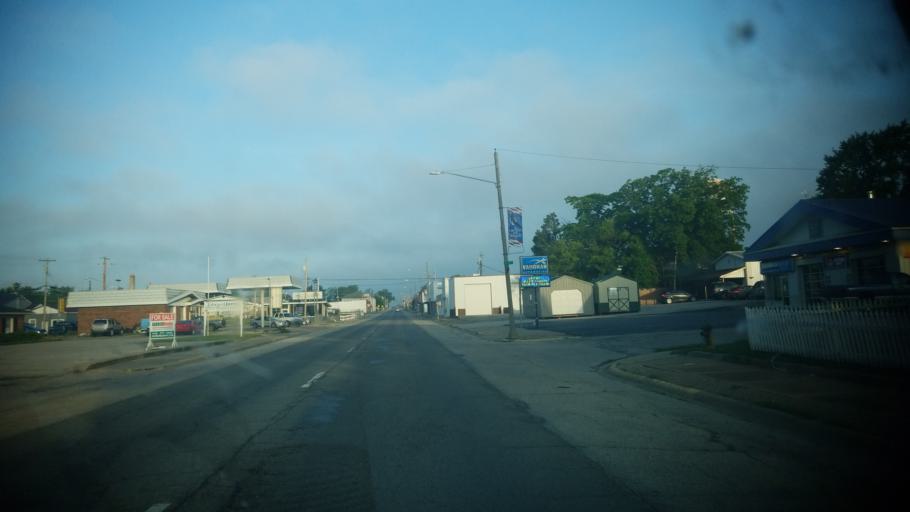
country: US
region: Illinois
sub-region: Wayne County
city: Fairfield
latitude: 38.3797
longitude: -88.3634
